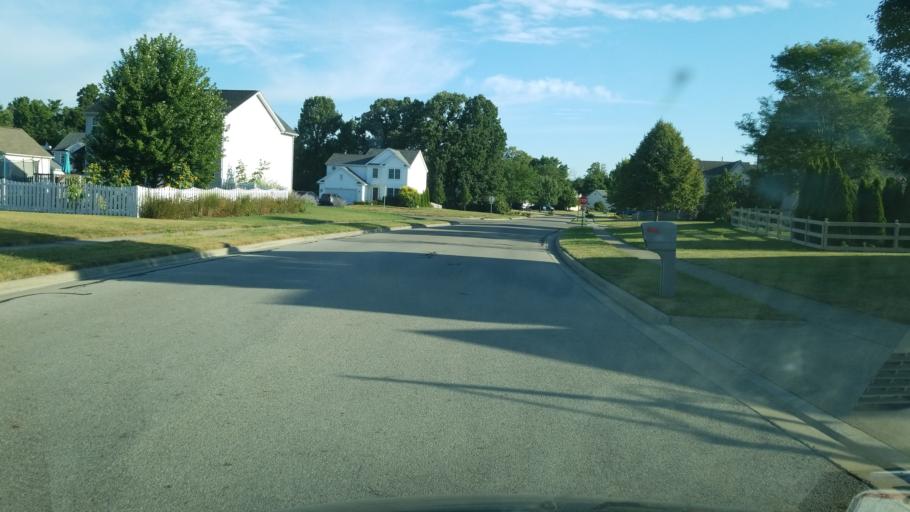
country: US
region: Ohio
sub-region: Delaware County
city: Lewis Center
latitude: 40.1694
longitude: -82.9982
